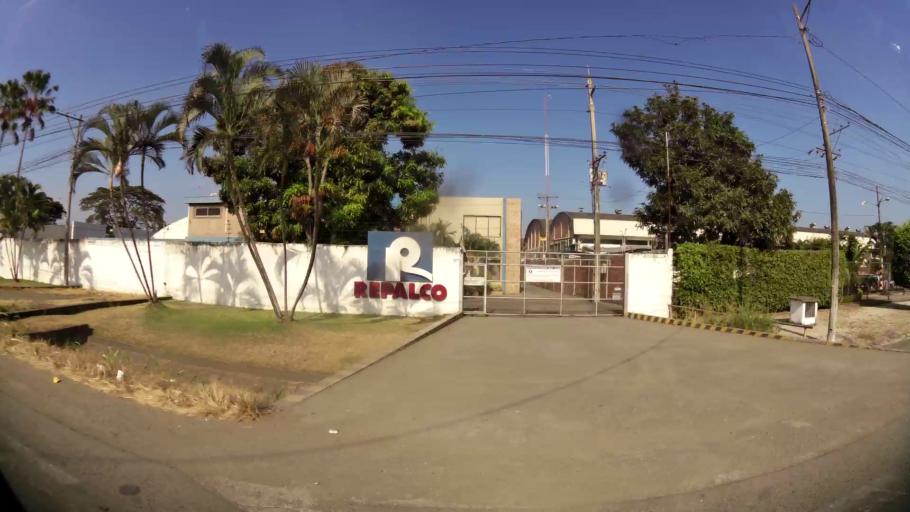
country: EC
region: Guayas
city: Eloy Alfaro
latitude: -2.1890
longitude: -79.8266
